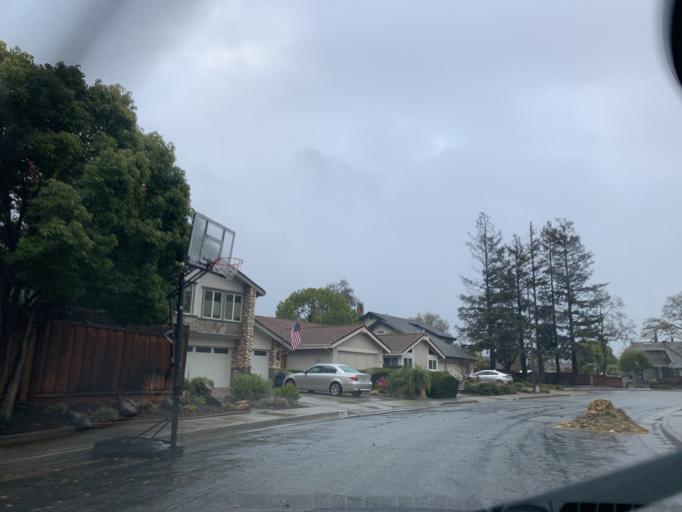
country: US
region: California
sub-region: Santa Clara County
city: Cambrian Park
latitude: 37.2574
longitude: -121.9443
